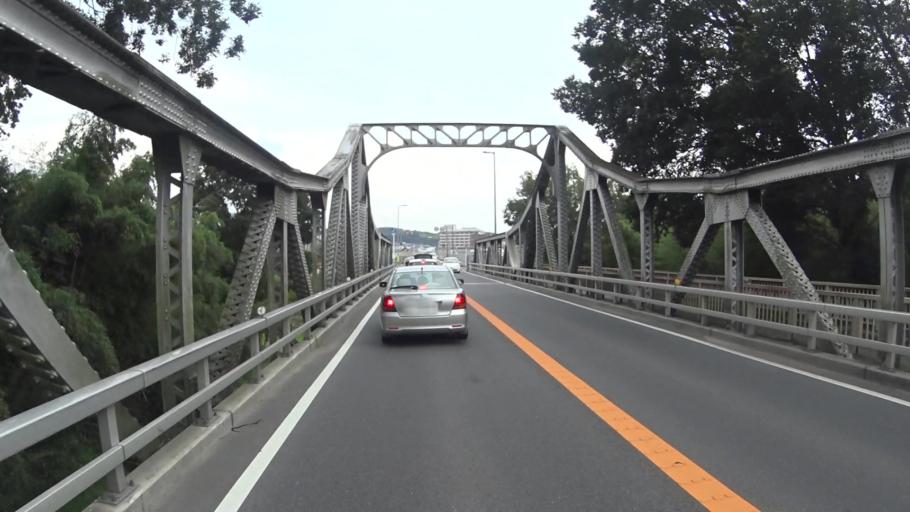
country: JP
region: Nara
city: Nara-shi
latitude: 34.7421
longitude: 135.8223
